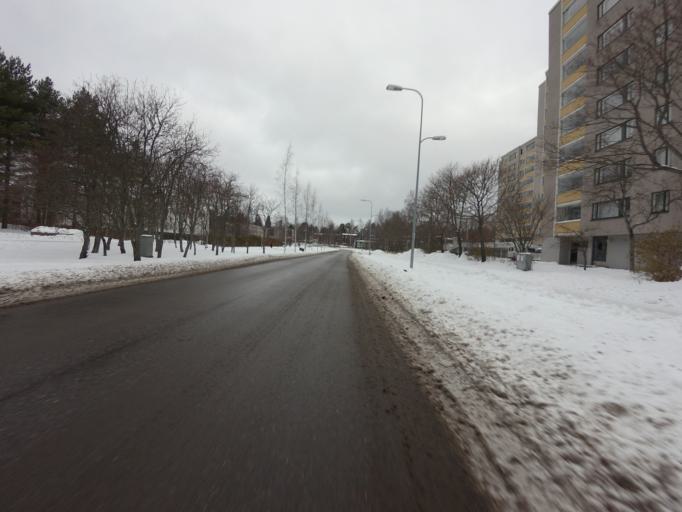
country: FI
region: Uusimaa
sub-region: Helsinki
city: Vantaa
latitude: 60.1821
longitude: 25.0582
